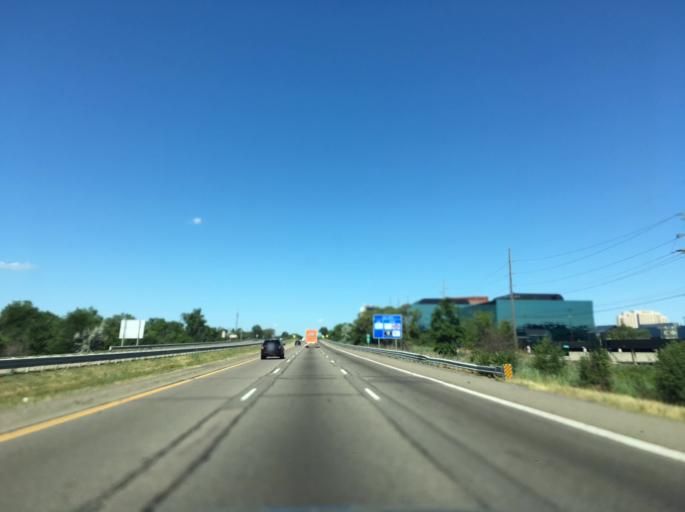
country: US
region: Michigan
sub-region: Oakland County
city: Clawson
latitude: 42.5593
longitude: -83.1412
